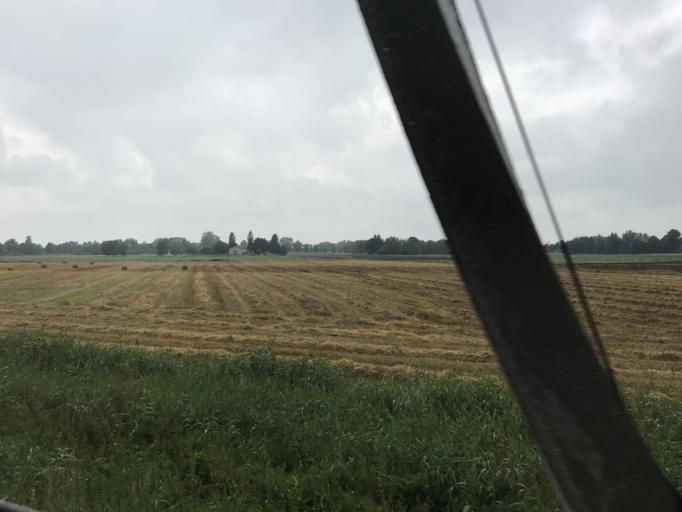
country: PL
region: Warmian-Masurian Voivodeship
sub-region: Powiat elblaski
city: Gronowo Elblaskie
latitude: 54.1133
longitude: 19.3471
